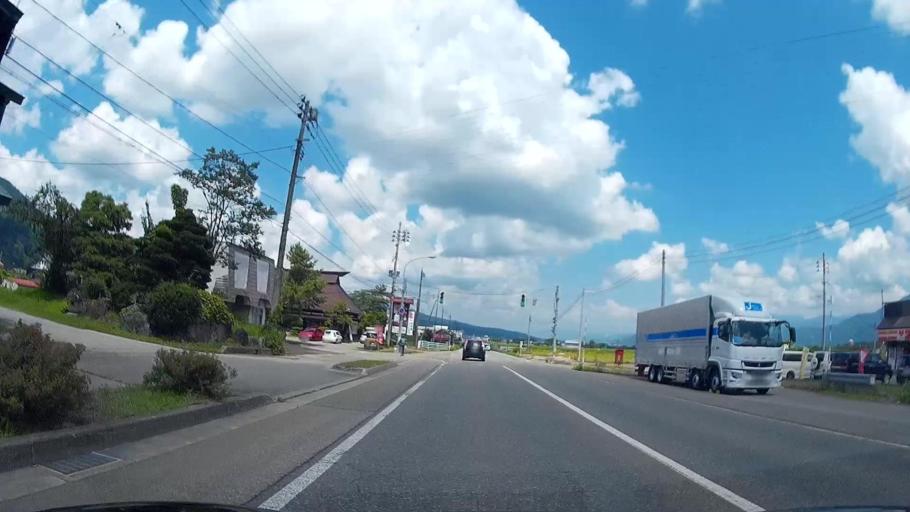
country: JP
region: Niigata
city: Shiozawa
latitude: 36.9949
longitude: 138.8125
